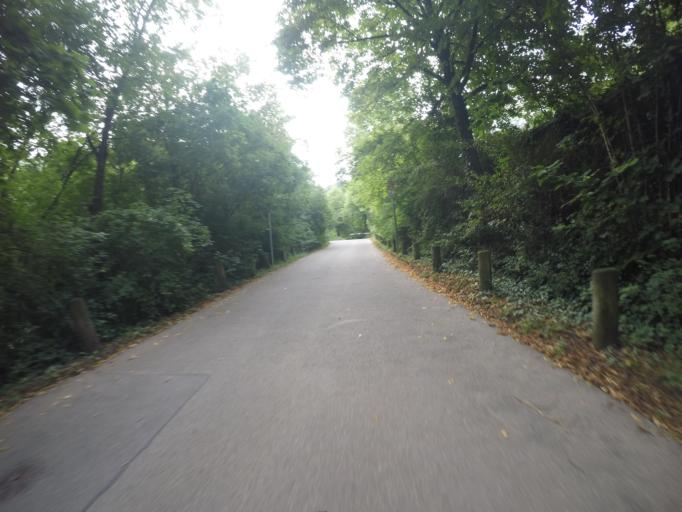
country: DE
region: Baden-Wuerttemberg
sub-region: Regierungsbezirk Stuttgart
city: Stuttgart
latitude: 48.7552
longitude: 9.1448
